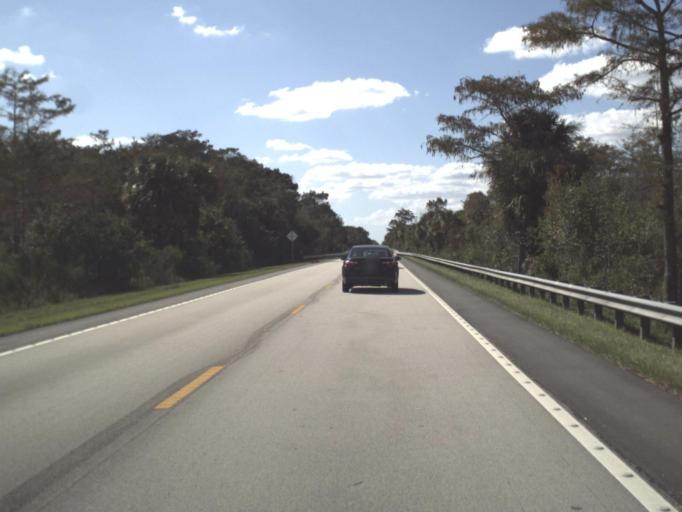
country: US
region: Florida
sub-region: Collier County
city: Marco
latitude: 25.8723
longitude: -81.1847
